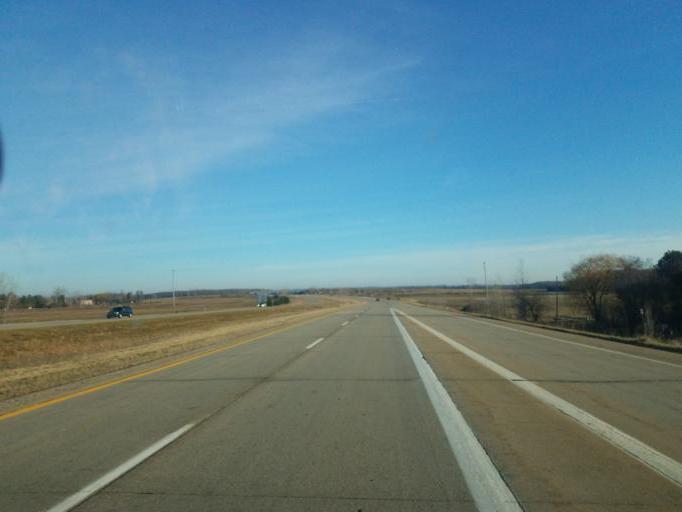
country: US
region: Michigan
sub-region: Clinton County
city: Saint Johns
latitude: 43.0075
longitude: -84.5187
